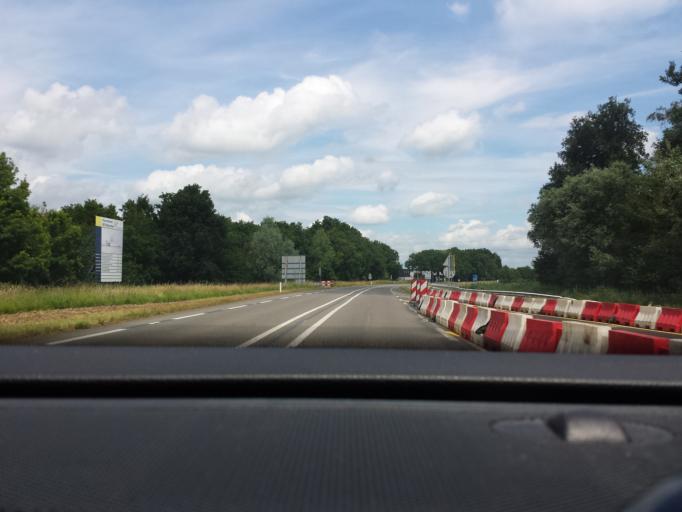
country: NL
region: Gelderland
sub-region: Berkelland
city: Borculo
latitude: 52.1178
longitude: 6.5376
